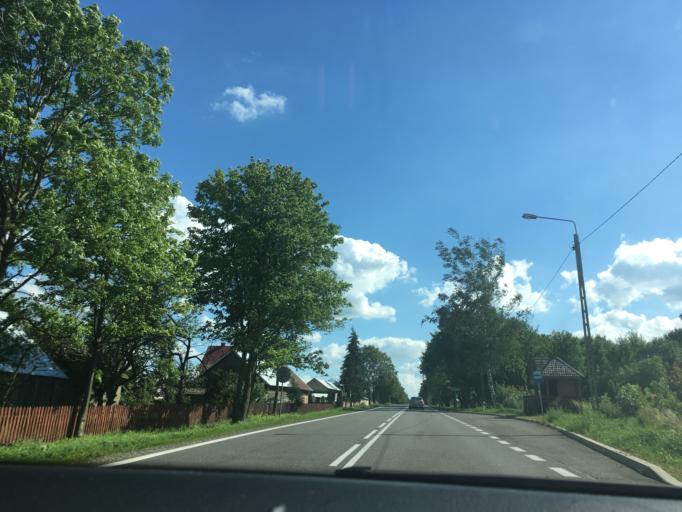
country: PL
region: Podlasie
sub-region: Powiat sokolski
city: Janow
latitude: 53.3772
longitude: 23.1102
